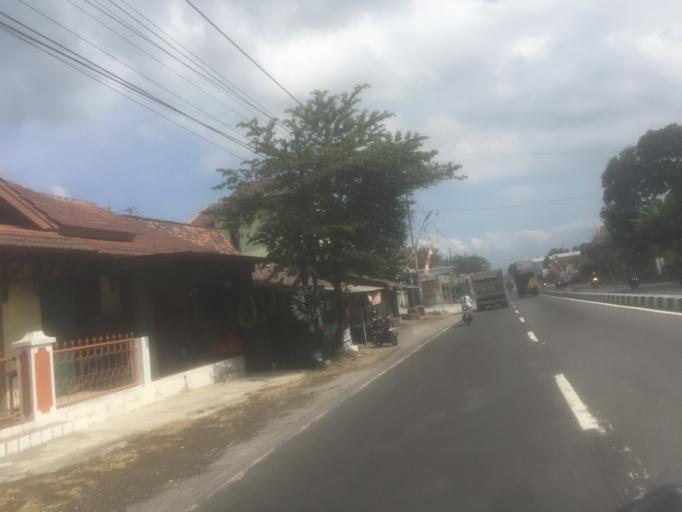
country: ID
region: Central Java
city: Muntilan
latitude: -7.6158
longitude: 110.3081
